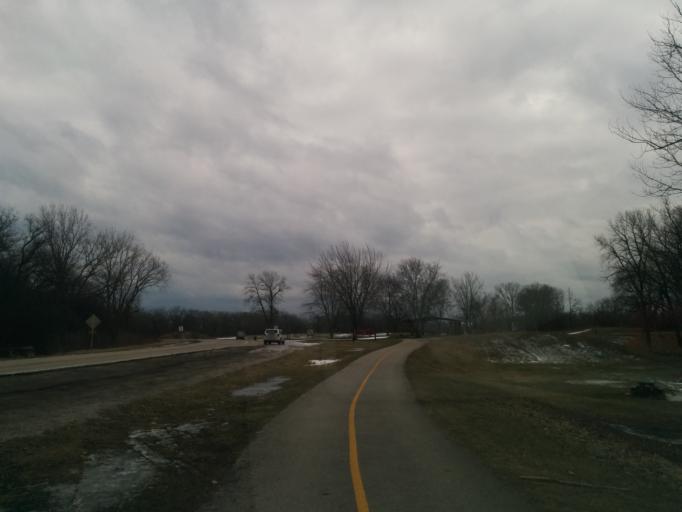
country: US
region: Illinois
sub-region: Cook County
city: Glencoe
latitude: 42.1299
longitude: -87.7754
